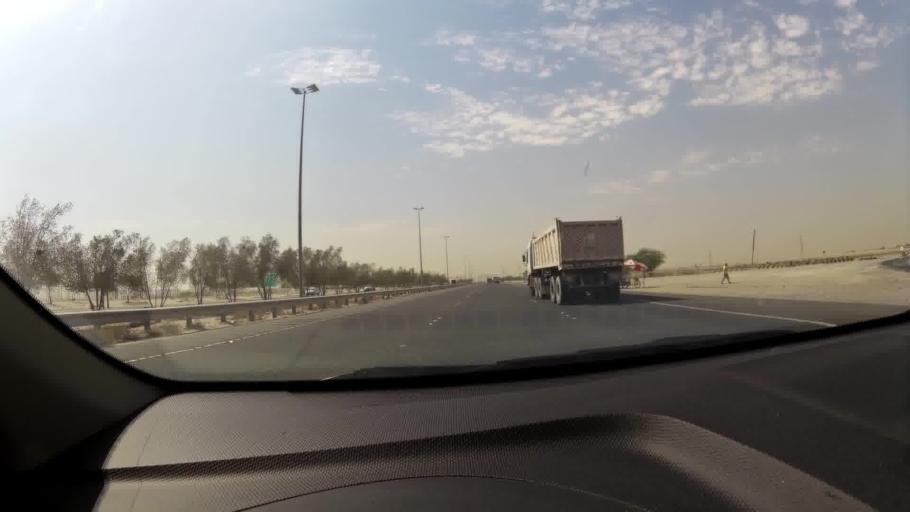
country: KW
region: Al Ahmadi
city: Al Fahahil
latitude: 28.7484
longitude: 48.2822
